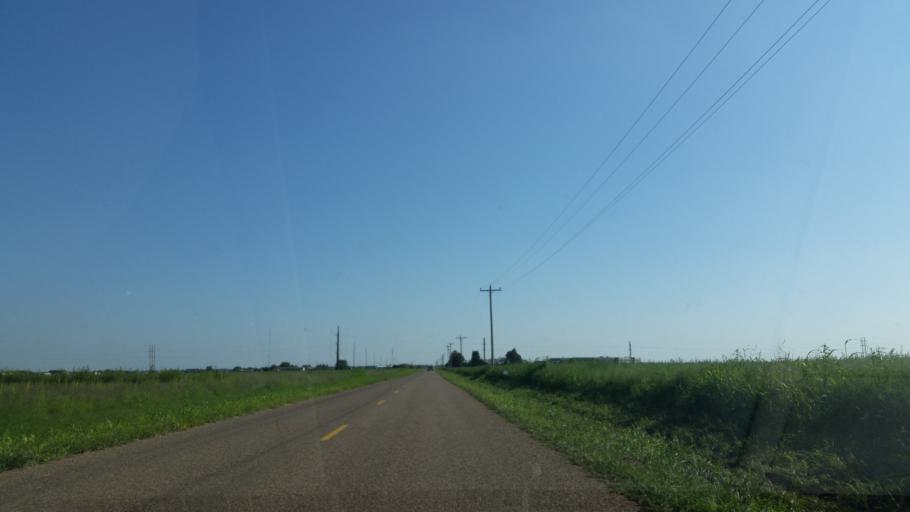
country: US
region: New Mexico
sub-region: Curry County
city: Clovis
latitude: 34.4604
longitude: -103.2141
